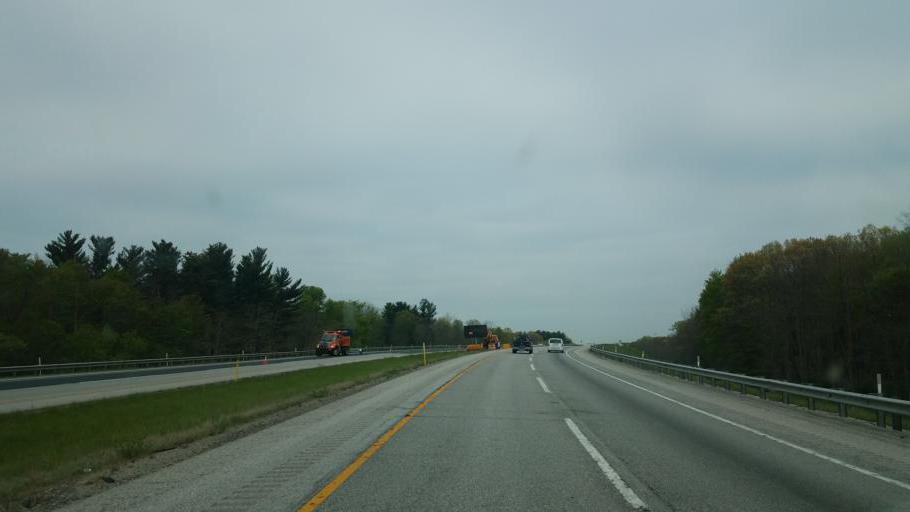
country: US
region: Indiana
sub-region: Elkhart County
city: Bristol
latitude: 41.7298
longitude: -85.7741
